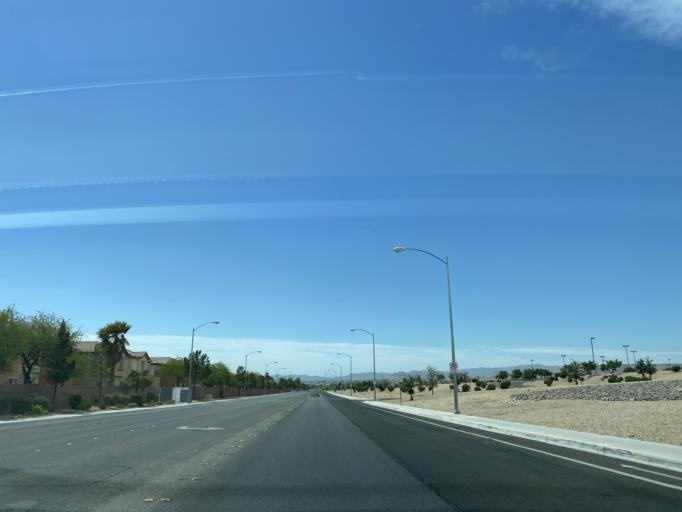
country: US
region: Nevada
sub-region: Clark County
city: Spring Valley
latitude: 36.1255
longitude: -115.2701
